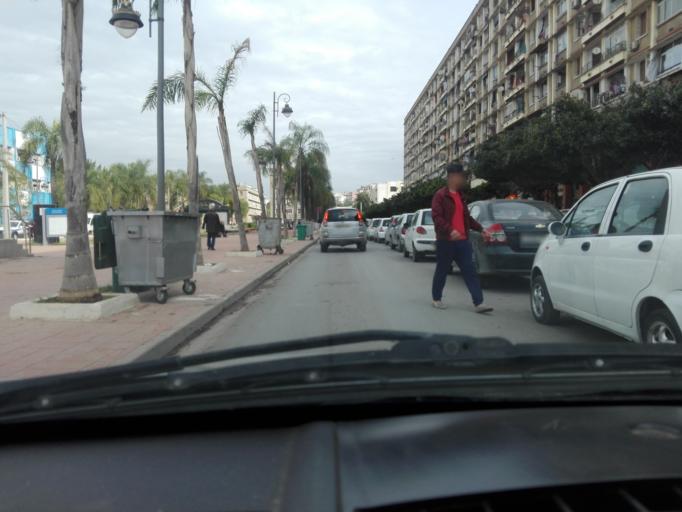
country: DZ
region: Alger
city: Bab Ezzouar
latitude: 36.7223
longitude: 3.1372
